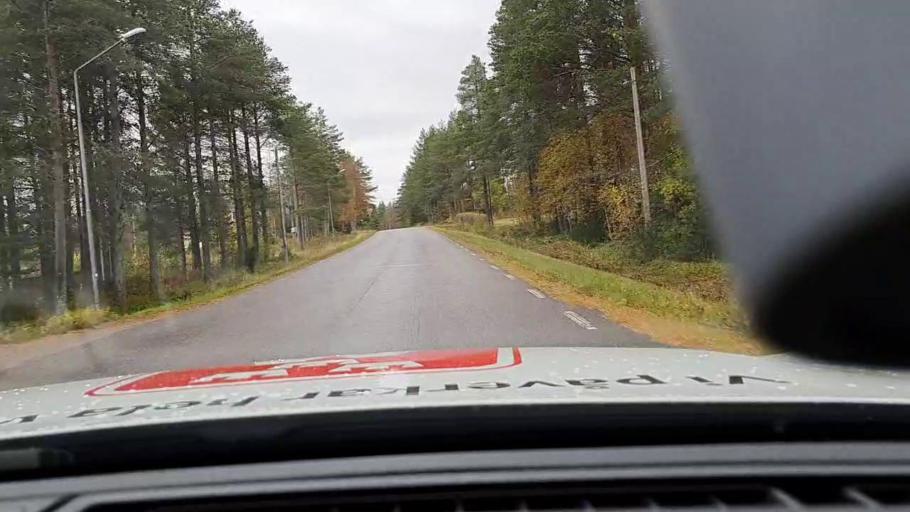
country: SE
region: Norrbotten
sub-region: Haparanda Kommun
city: Haparanda
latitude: 65.7836
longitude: 23.9198
